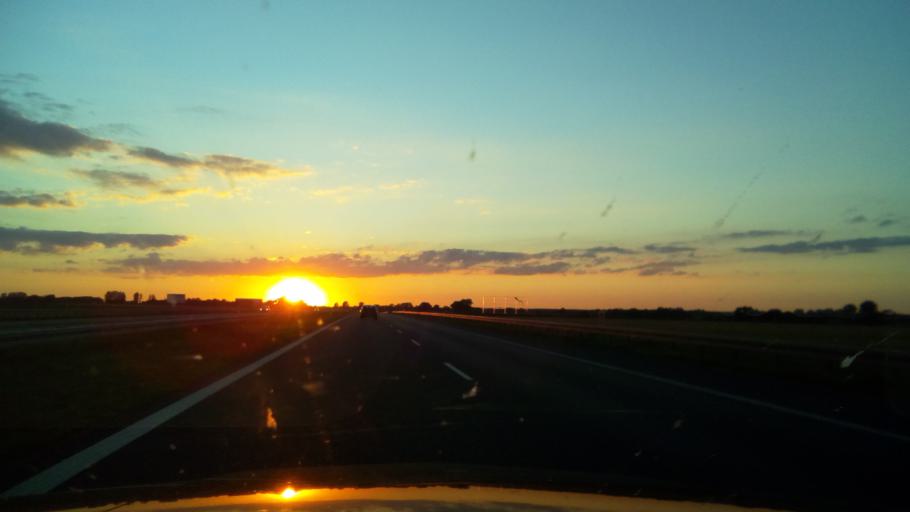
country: PL
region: Lodz Voivodeship
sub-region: Powiat poddebicki
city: Wartkowice
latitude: 51.9795
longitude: 19.0742
